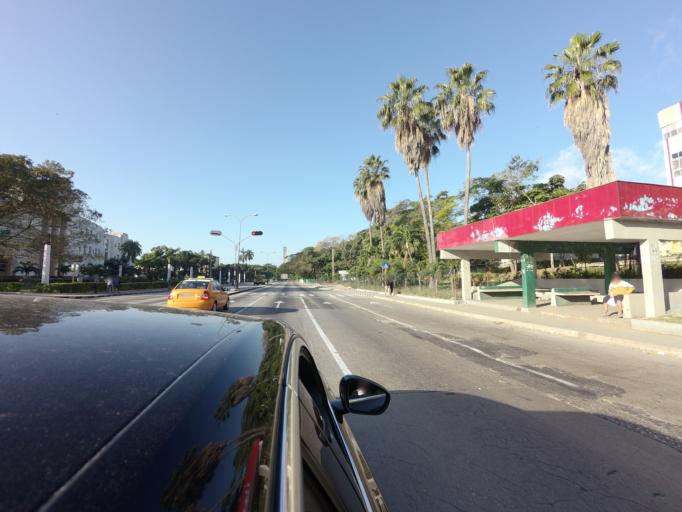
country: CU
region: La Habana
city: Cerro
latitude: 23.0894
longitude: -82.4245
